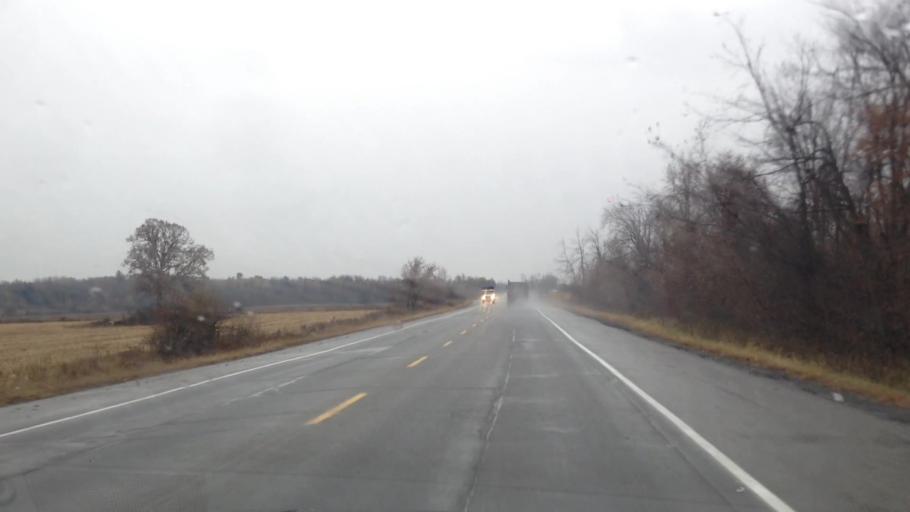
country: CA
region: Ontario
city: Clarence-Rockland
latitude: 45.3888
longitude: -75.3896
